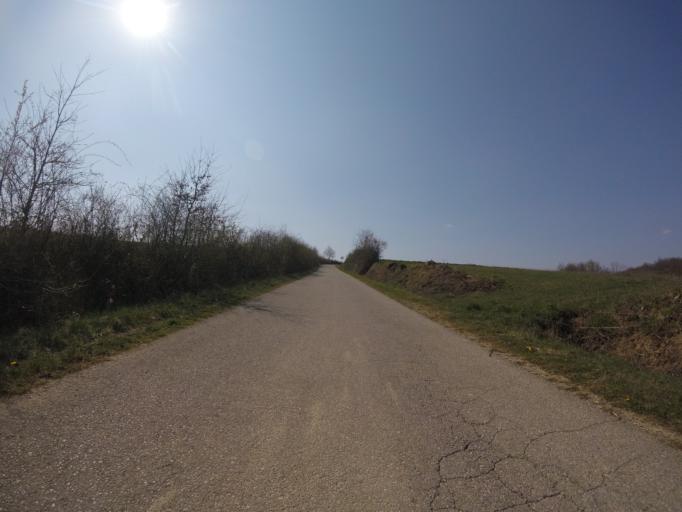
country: HR
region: Grad Zagreb
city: Strmec
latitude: 45.5592
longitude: 15.9124
